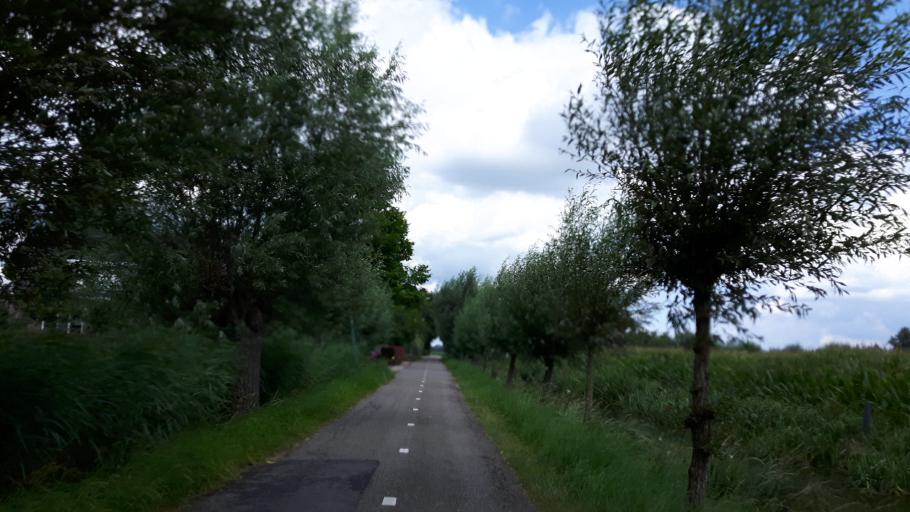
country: NL
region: Utrecht
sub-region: Gemeente Woerden
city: Woerden
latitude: 52.1050
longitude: 4.9229
